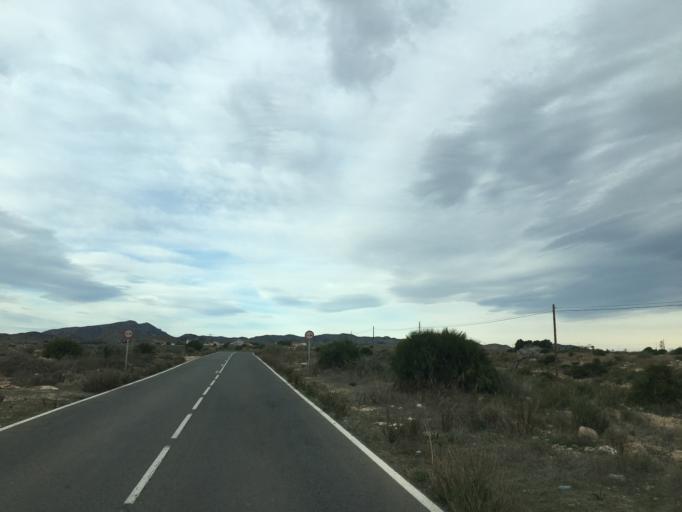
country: ES
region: Murcia
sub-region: Murcia
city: Fuente-Alamo de Murcia
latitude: 37.6194
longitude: -1.0753
